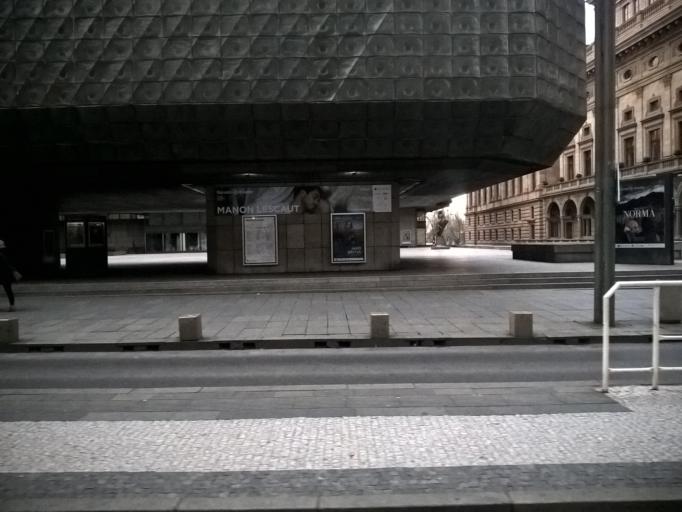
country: CZ
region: Praha
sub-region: Praha 1
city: Stare Mesto
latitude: 50.0814
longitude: 14.4141
